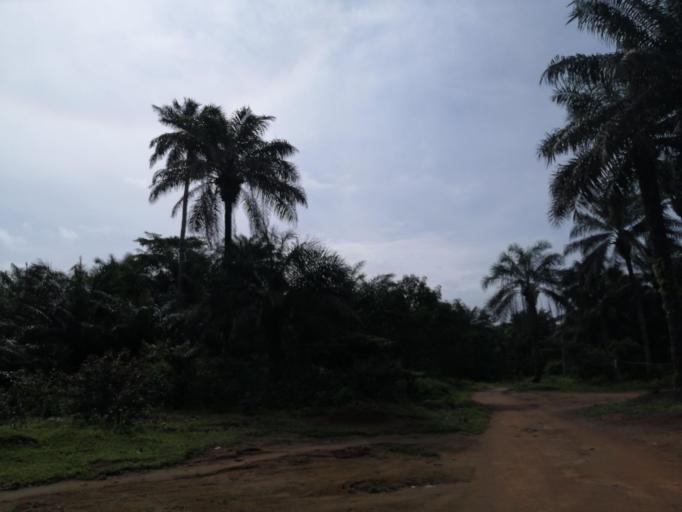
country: SL
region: Northern Province
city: Port Loko
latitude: 8.7893
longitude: -12.9277
